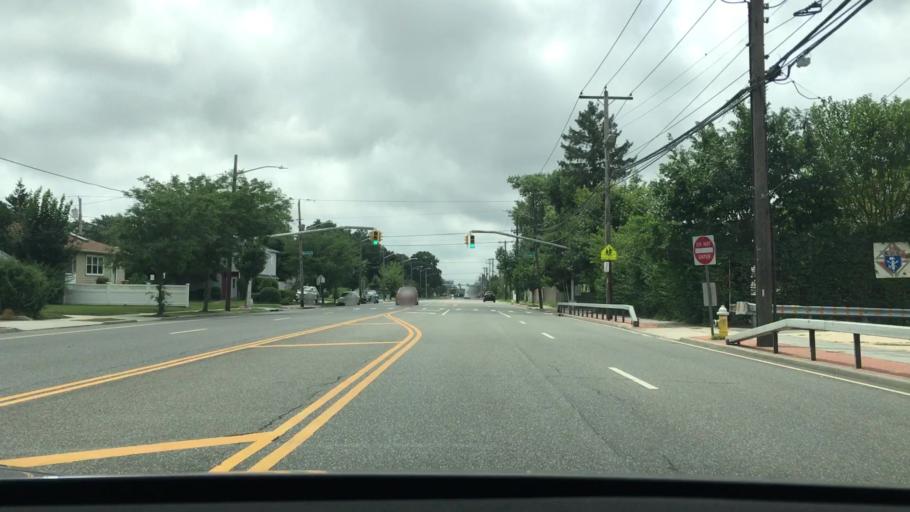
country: US
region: New York
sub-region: Nassau County
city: Hicksville
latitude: 40.7748
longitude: -73.5020
